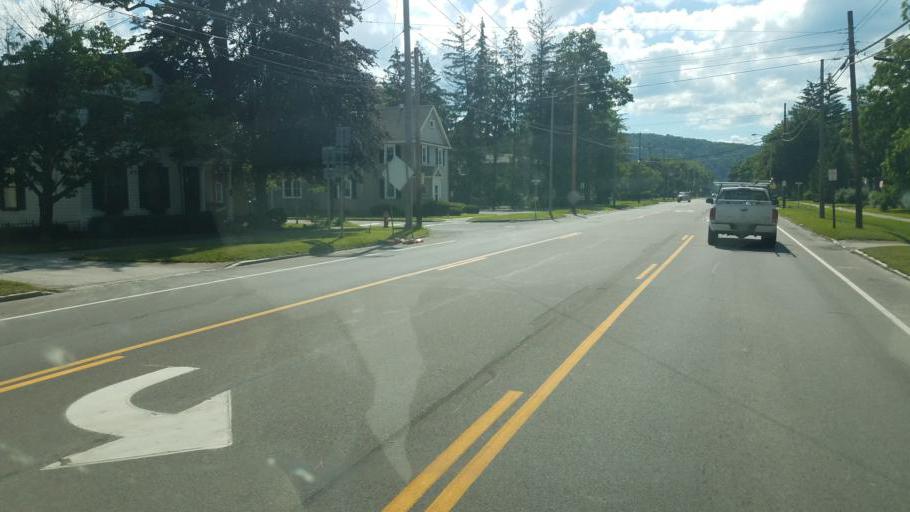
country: US
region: New York
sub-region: Steuben County
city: Bath
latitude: 42.3372
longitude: -77.3201
